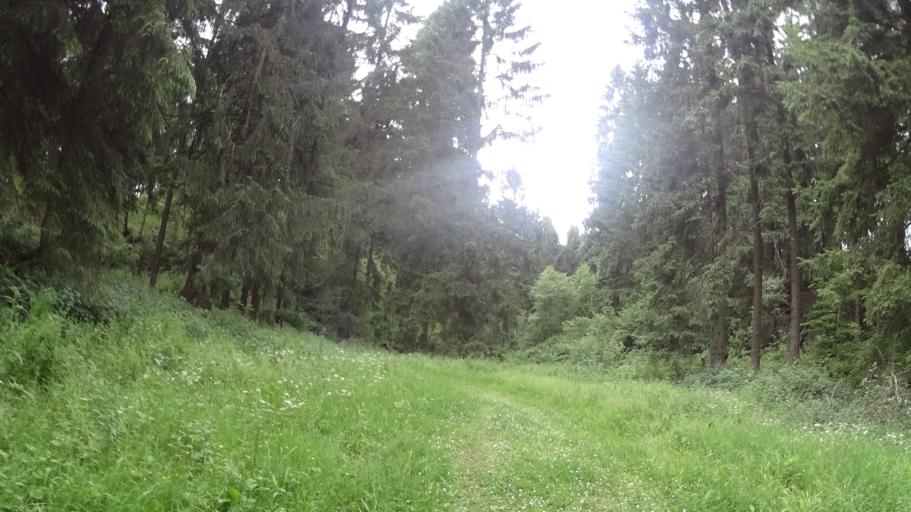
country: DE
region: Lower Saxony
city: Hameln
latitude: 52.1613
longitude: 9.3981
